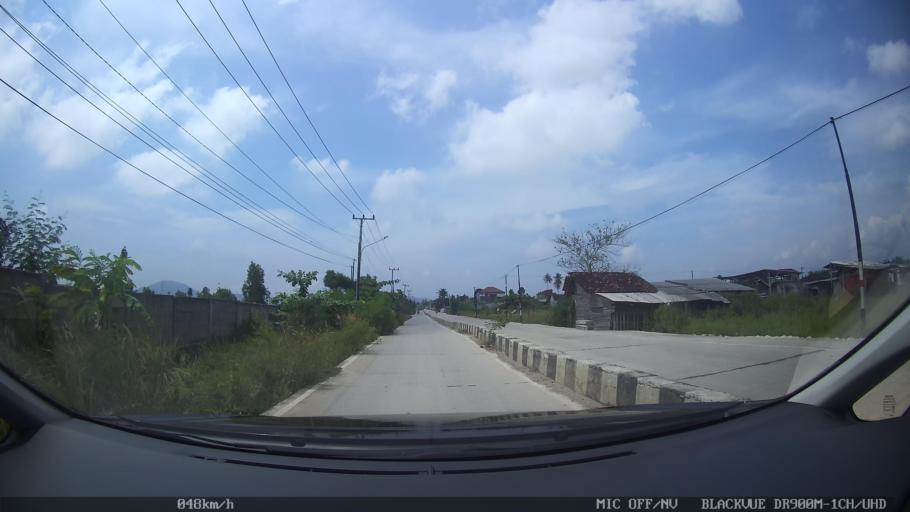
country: ID
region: Lampung
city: Kedaton
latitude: -5.3685
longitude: 105.3085
